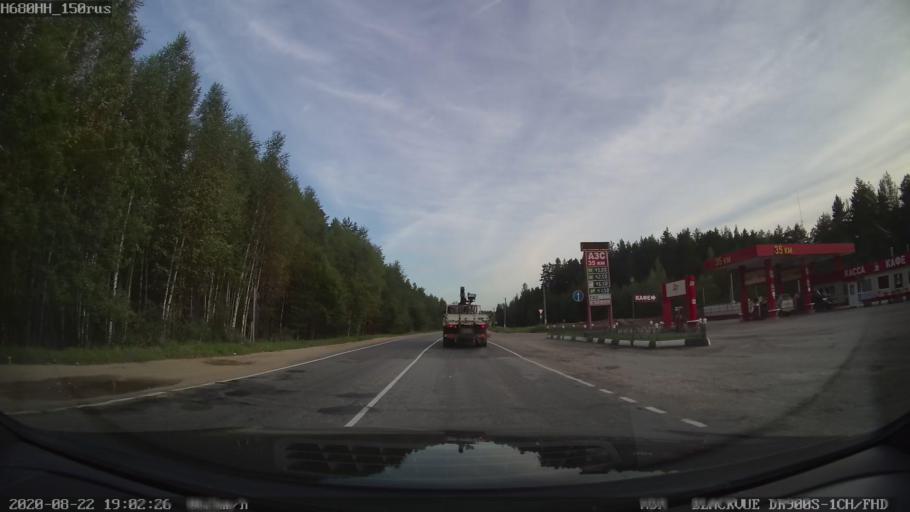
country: RU
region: Tverskaya
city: Sakharovo
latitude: 57.1087
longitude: 36.1201
